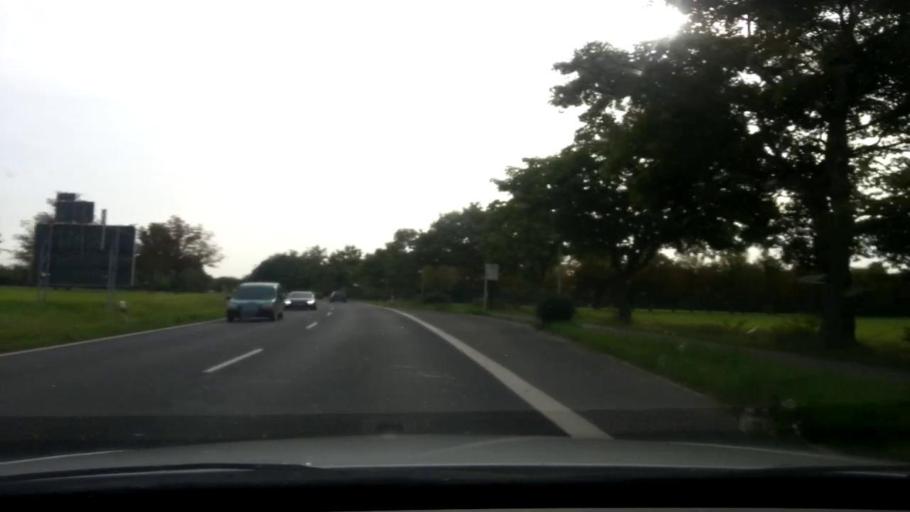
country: DE
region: Bavaria
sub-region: Upper Franconia
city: Memmelsdorf
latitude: 49.9291
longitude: 10.9431
